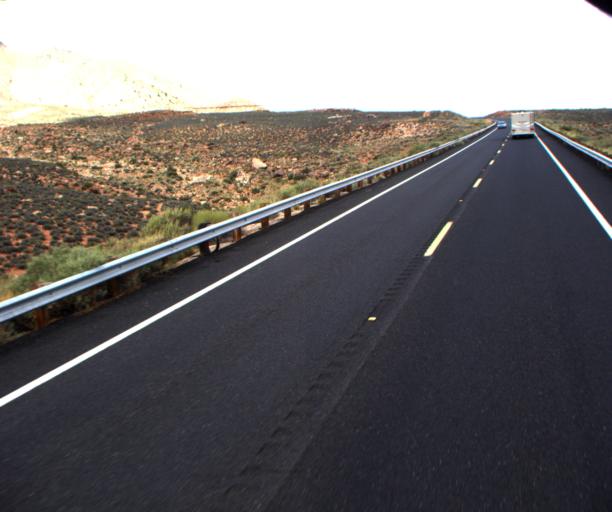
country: US
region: Arizona
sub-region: Coconino County
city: Tuba City
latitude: 35.9281
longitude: -111.6168
